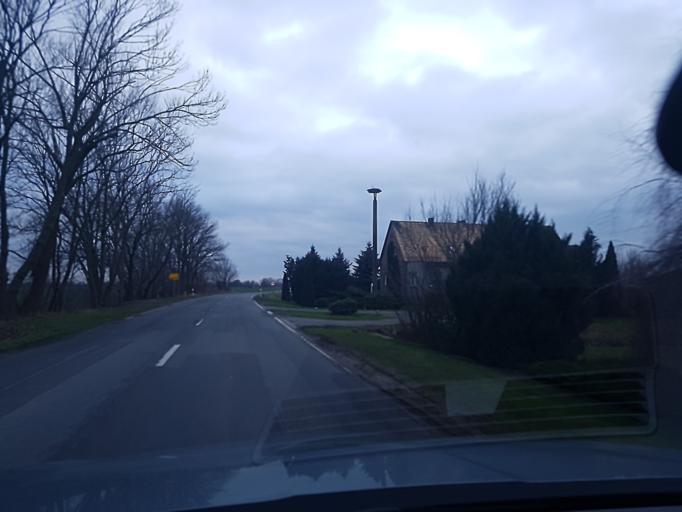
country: DE
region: Brandenburg
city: Schonewalde
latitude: 51.6770
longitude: 13.5977
